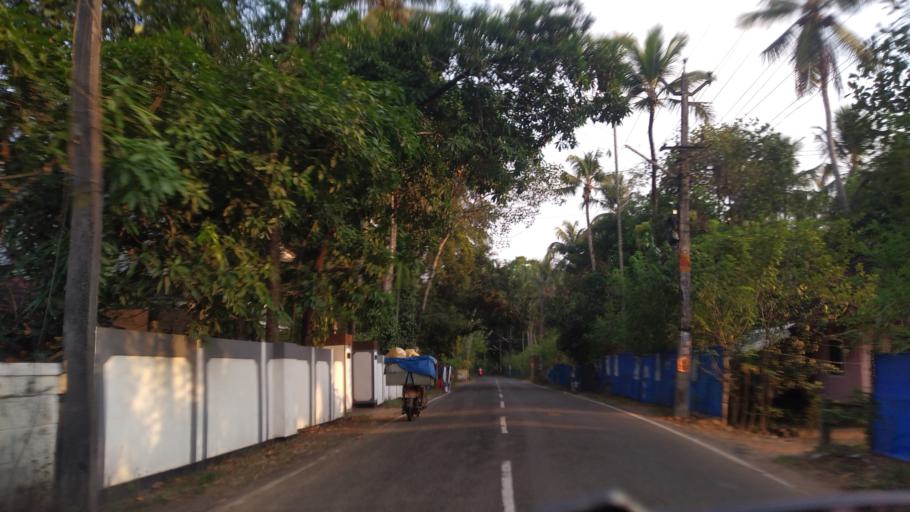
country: IN
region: Kerala
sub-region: Thrissur District
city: Thanniyam
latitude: 10.3789
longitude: 76.1017
